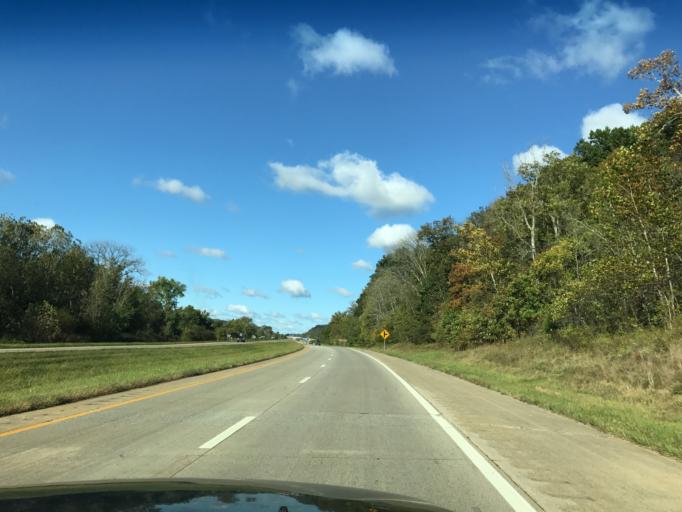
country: US
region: Ohio
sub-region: Athens County
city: Athens
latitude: 39.3342
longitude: -82.0111
